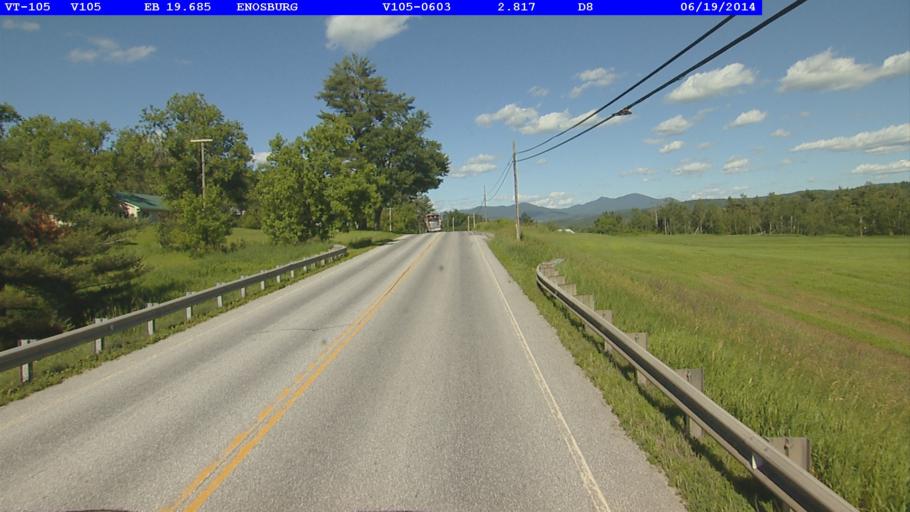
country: US
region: Vermont
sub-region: Franklin County
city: Enosburg Falls
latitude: 44.9180
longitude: -72.7711
